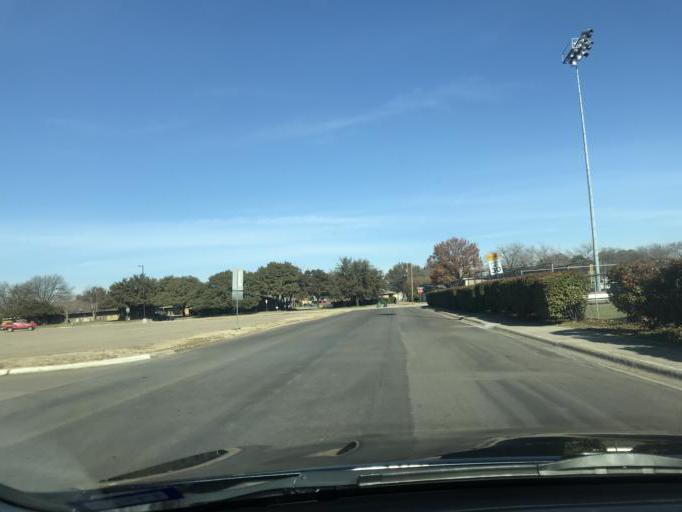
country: US
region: Texas
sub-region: Denton County
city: Denton
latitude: 33.2246
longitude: -97.1475
